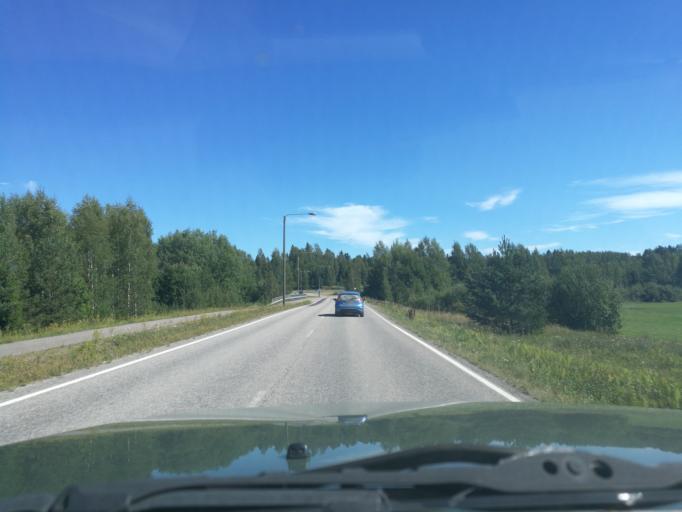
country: FI
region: Uusimaa
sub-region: Helsinki
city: Kerava
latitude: 60.3602
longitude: 25.1220
